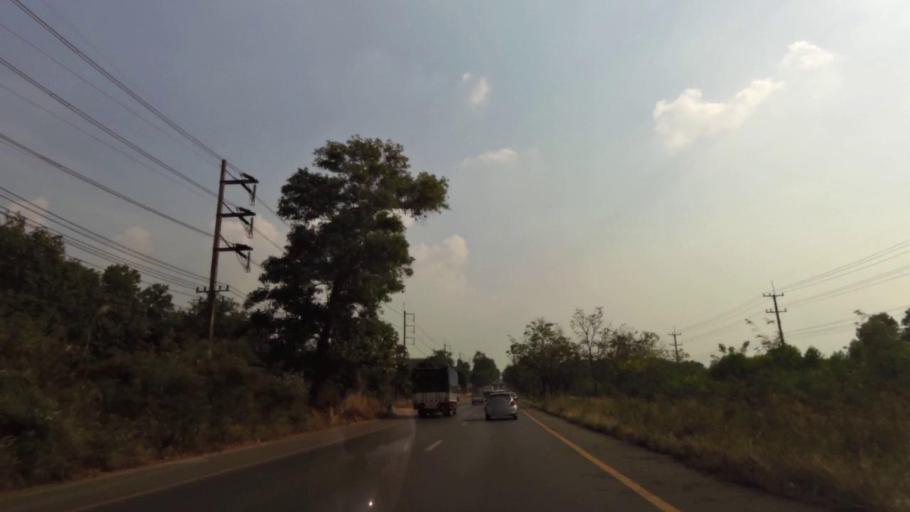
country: TH
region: Rayong
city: Wang Chan
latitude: 12.9230
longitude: 101.5278
